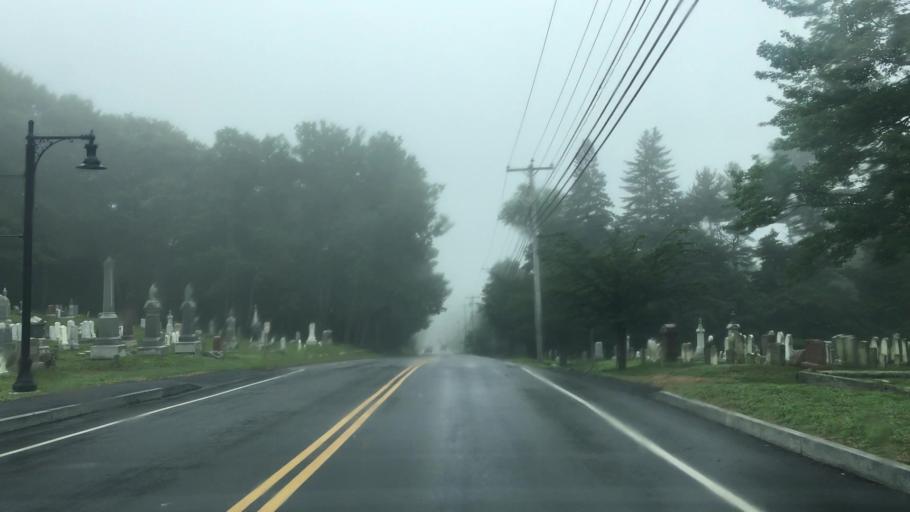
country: US
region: Maine
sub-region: Lincoln County
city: Boothbay
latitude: 43.8741
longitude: -69.6333
